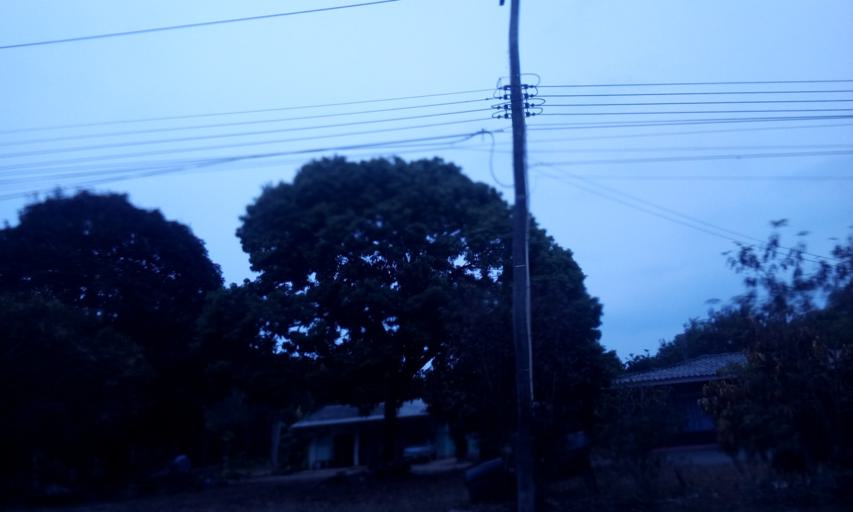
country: TH
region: Trat
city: Laem Ngop
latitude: 12.2381
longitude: 102.2965
